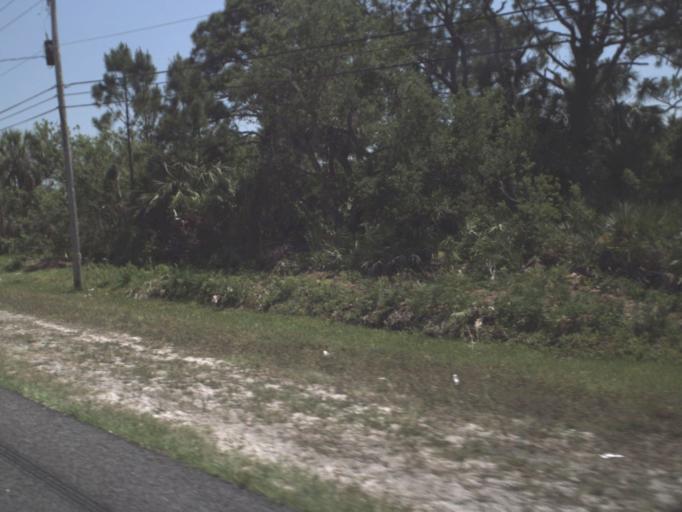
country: US
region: Florida
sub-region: Brevard County
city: Grant-Valkaria
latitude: 27.9540
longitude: -80.5373
